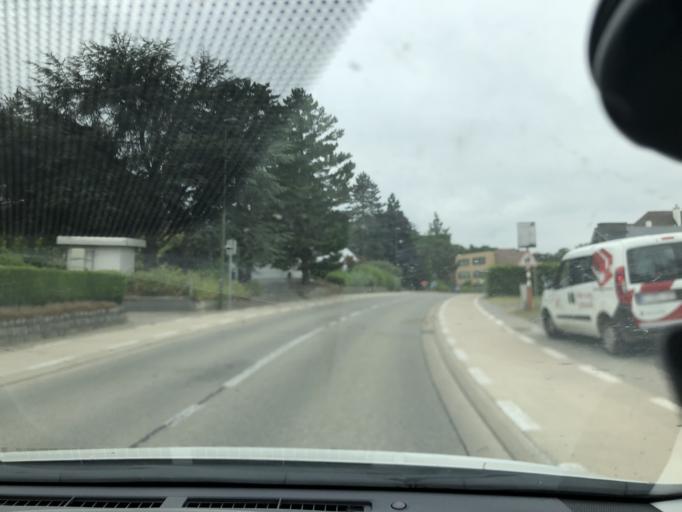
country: BE
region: Flanders
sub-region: Provincie Vlaams-Brabant
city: Oud-Heverlee
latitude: 50.8376
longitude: 4.6664
